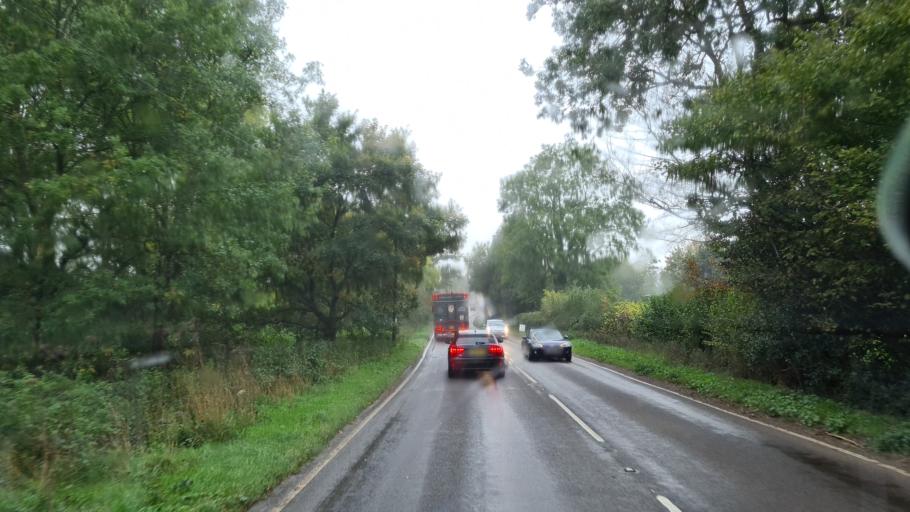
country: GB
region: England
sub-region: West Sussex
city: Ashington
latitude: 50.9099
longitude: -0.3779
